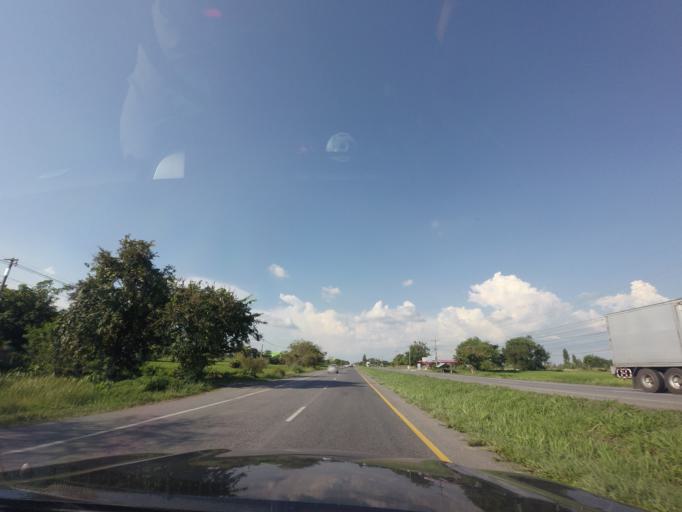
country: TH
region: Khon Kaen
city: Non Sila
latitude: 16.0003
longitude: 102.7017
